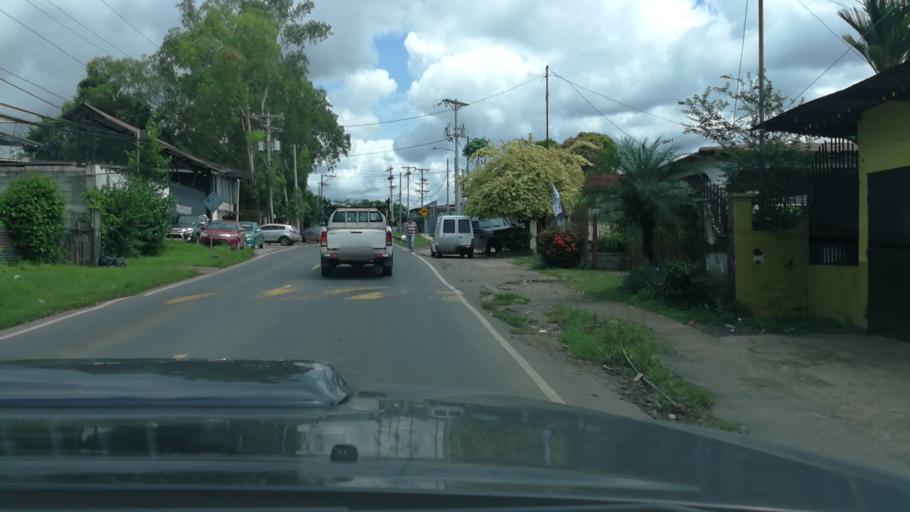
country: PA
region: Panama
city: Tocumen
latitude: 9.0735
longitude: -79.4274
